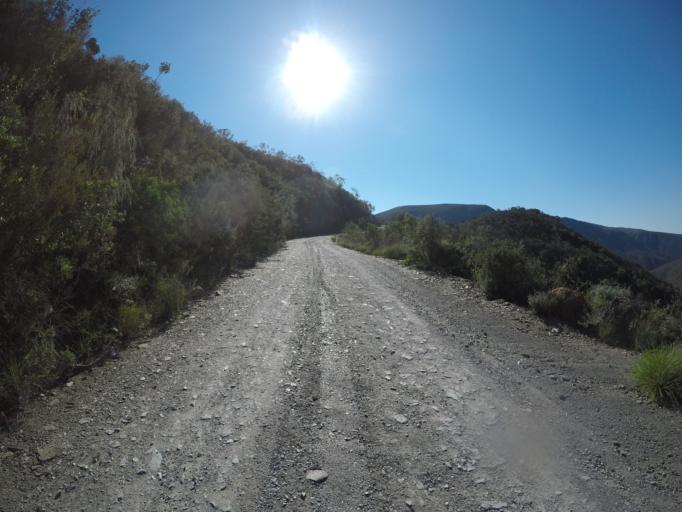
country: ZA
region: Eastern Cape
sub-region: Cacadu District Municipality
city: Kareedouw
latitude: -33.6545
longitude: 24.5080
